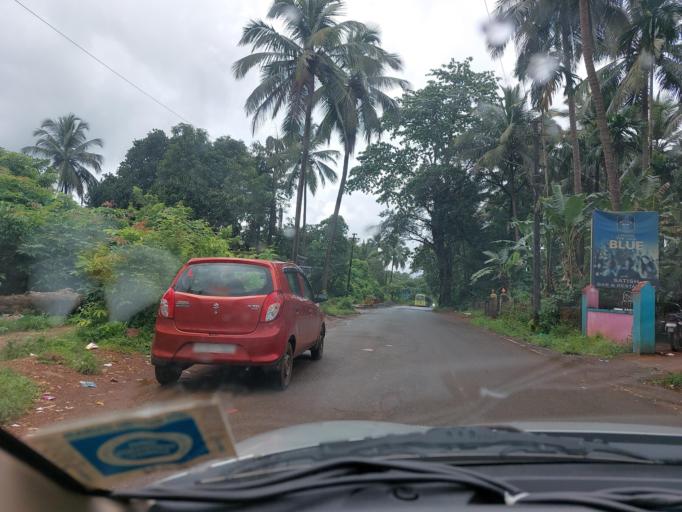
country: IN
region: Goa
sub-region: North Goa
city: Valpoy
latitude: 15.5393
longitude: 74.1373
